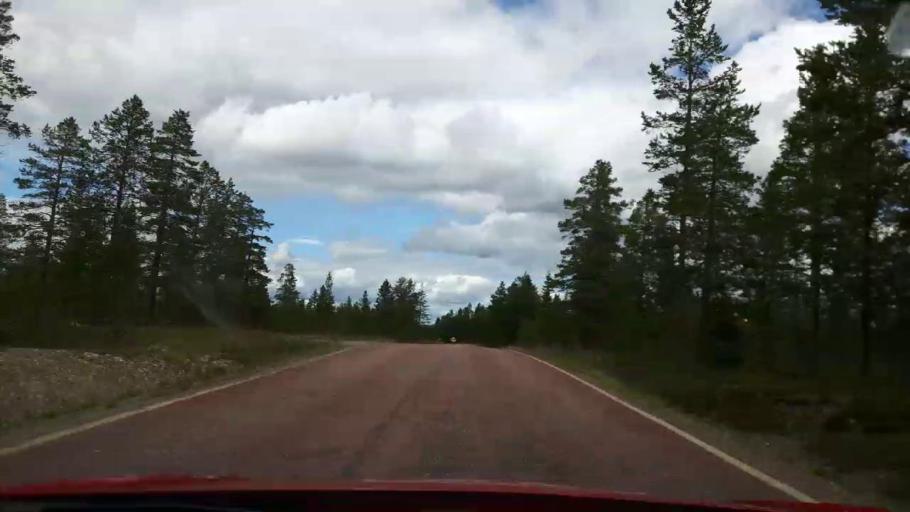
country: NO
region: Hedmark
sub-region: Trysil
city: Innbygda
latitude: 61.9231
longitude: 13.0170
